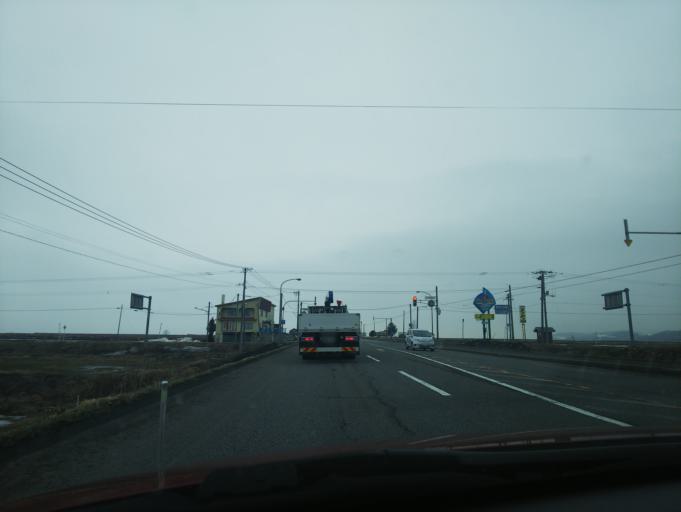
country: JP
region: Hokkaido
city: Nayoro
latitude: 44.0698
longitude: 142.3952
